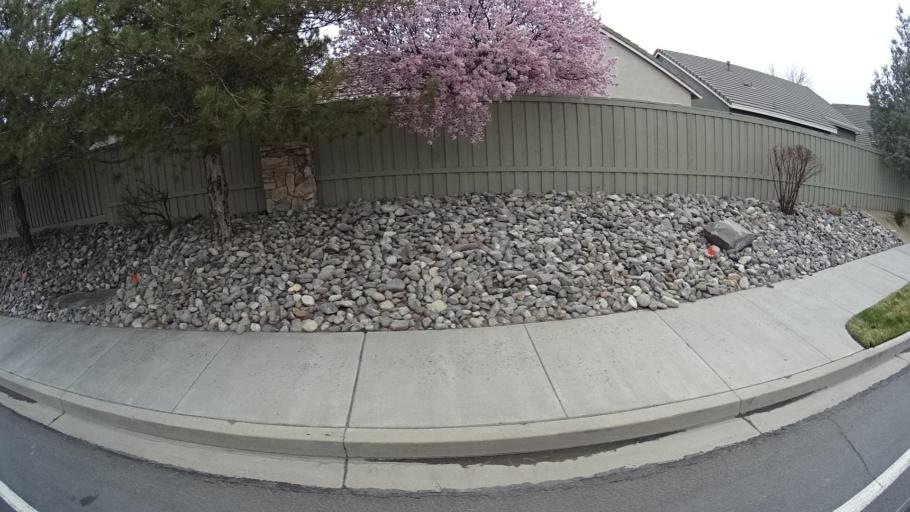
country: US
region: Nevada
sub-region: Washoe County
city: Sparks
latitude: 39.4342
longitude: -119.7446
